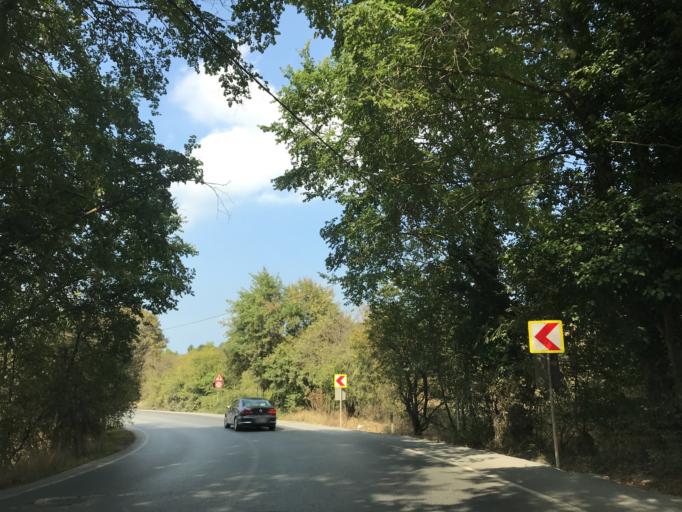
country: TR
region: Istanbul
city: Arikoey
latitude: 41.2157
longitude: 29.0351
